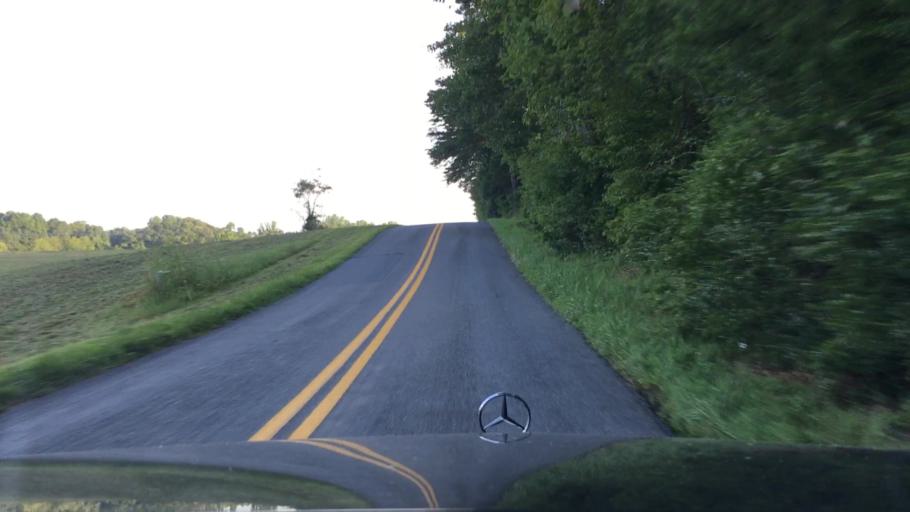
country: US
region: Virginia
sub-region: Campbell County
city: Timberlake
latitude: 37.2736
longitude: -79.2667
